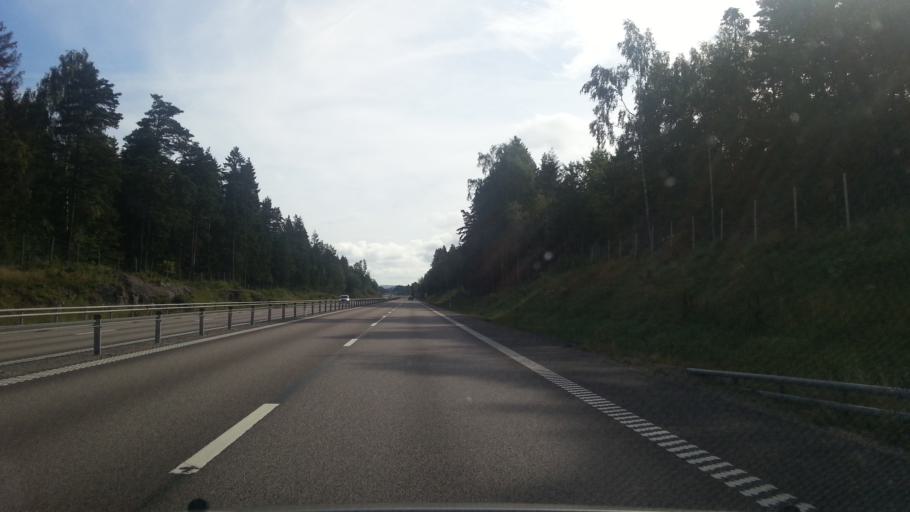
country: SE
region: Vaestra Goetaland
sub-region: Trollhattan
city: Sjuntorp
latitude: 58.2407
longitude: 12.2451
